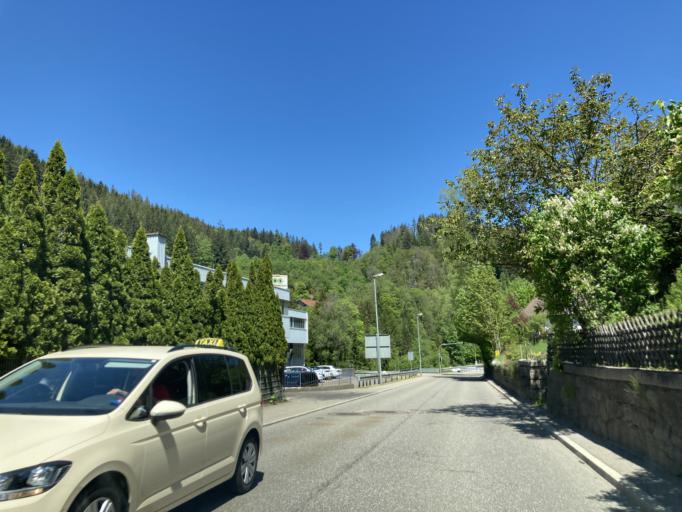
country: DE
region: Baden-Wuerttemberg
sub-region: Freiburg Region
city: Triberg im Schwarzwald
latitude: 48.1403
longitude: 8.2388
